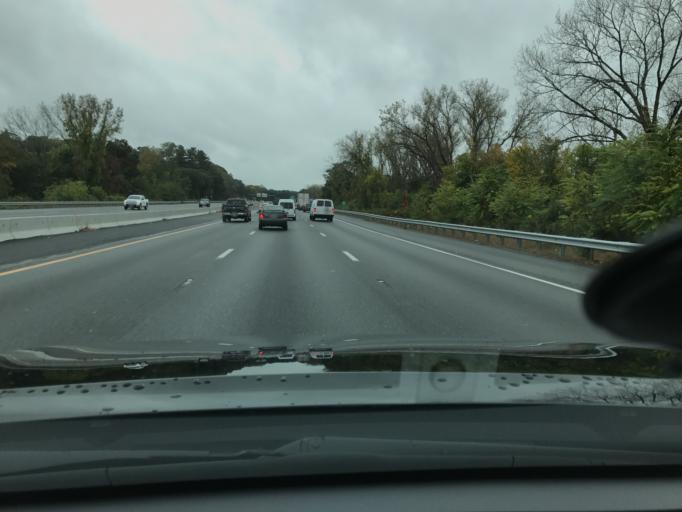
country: US
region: Massachusetts
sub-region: Middlesex County
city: Reading
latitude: 42.5127
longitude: -71.0916
